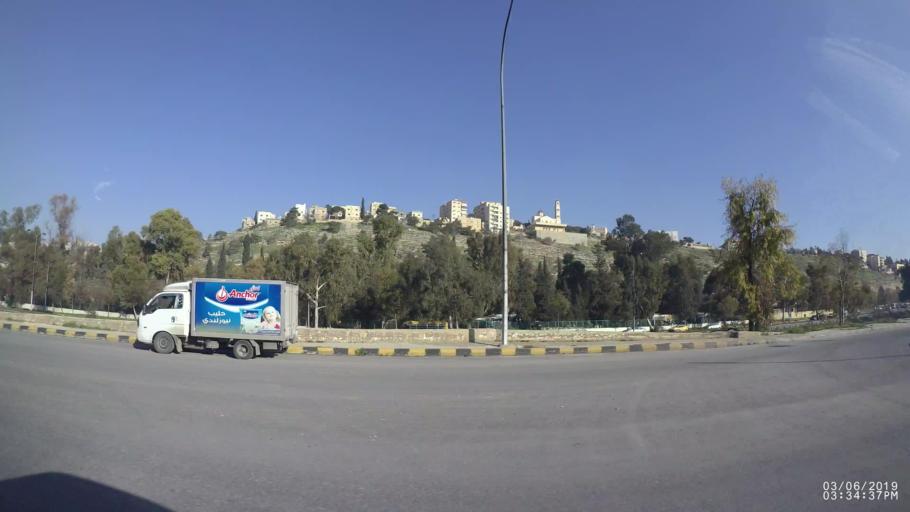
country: JO
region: Amman
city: Amman
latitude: 31.9780
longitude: 35.9714
